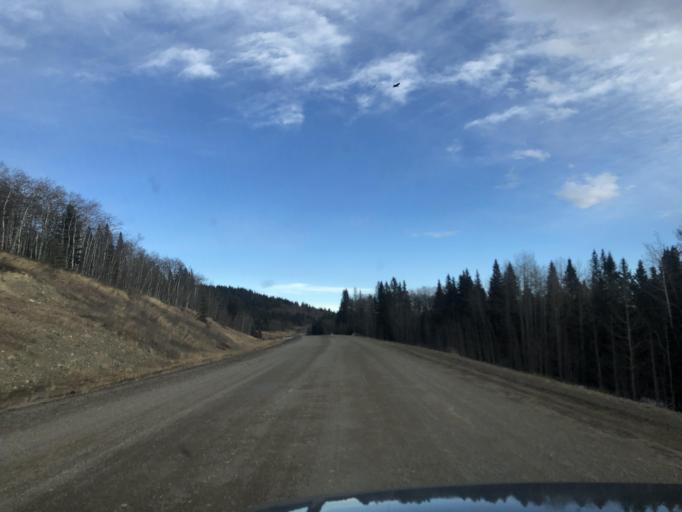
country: CA
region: Alberta
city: Cochrane
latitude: 51.0436
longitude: -114.7680
